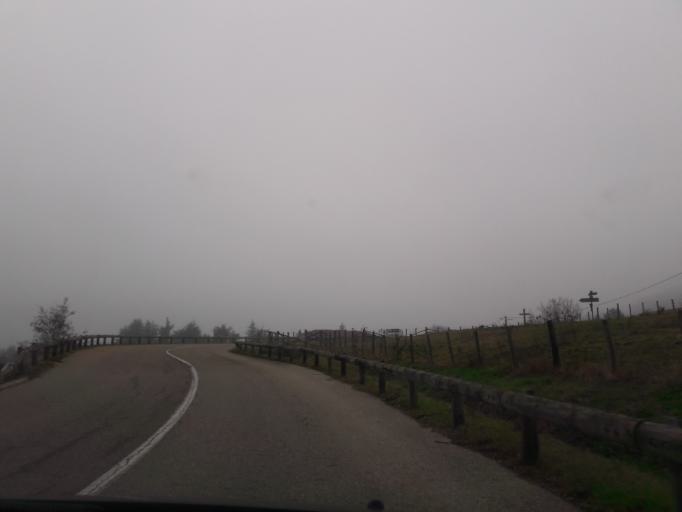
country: FR
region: Rhone-Alpes
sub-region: Departement de l'Isere
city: Chatonnay
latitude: 45.4263
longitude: 5.1818
